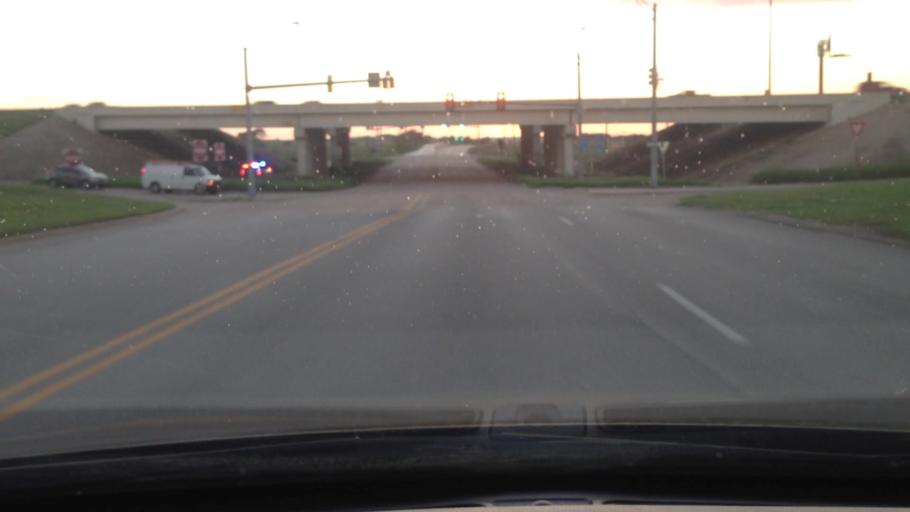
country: US
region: Texas
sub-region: Tarrant County
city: White Settlement
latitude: 32.7743
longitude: -97.4737
